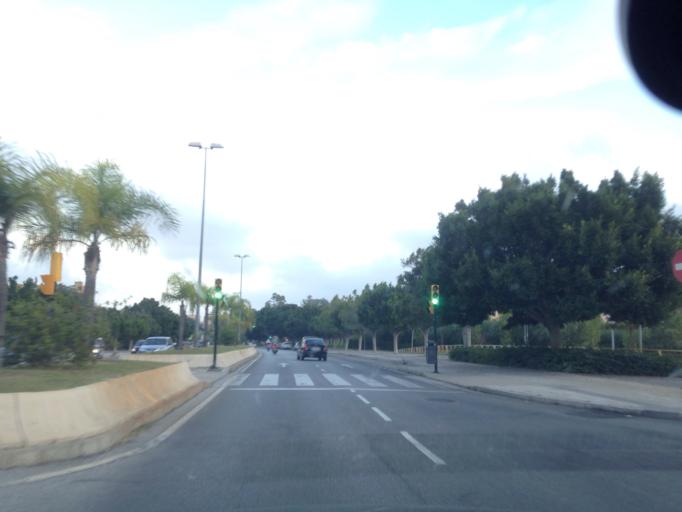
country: ES
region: Andalusia
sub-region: Provincia de Malaga
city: Malaga
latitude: 36.7272
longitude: -4.4631
